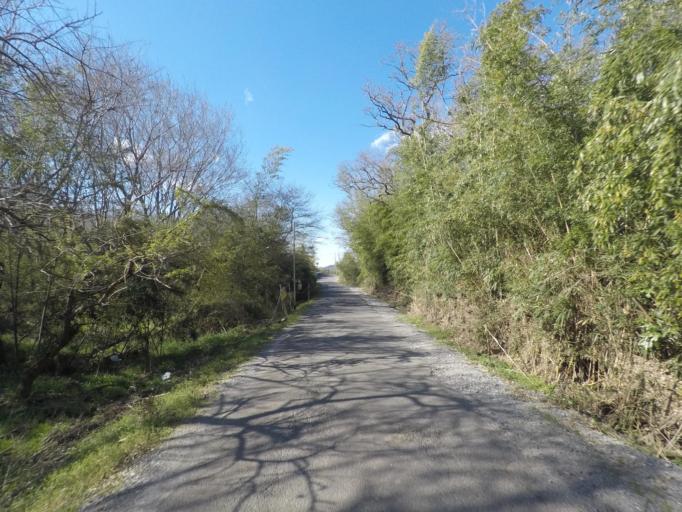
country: JP
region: Ibaraki
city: Tsukuba
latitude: 36.1438
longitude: 140.1117
